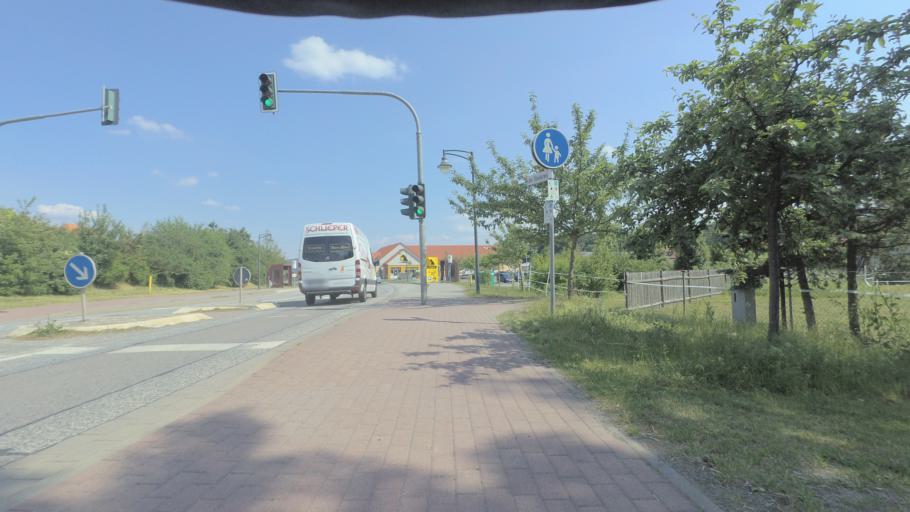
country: DE
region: Saxony-Anhalt
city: Darlingerode
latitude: 51.8492
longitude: 10.7361
